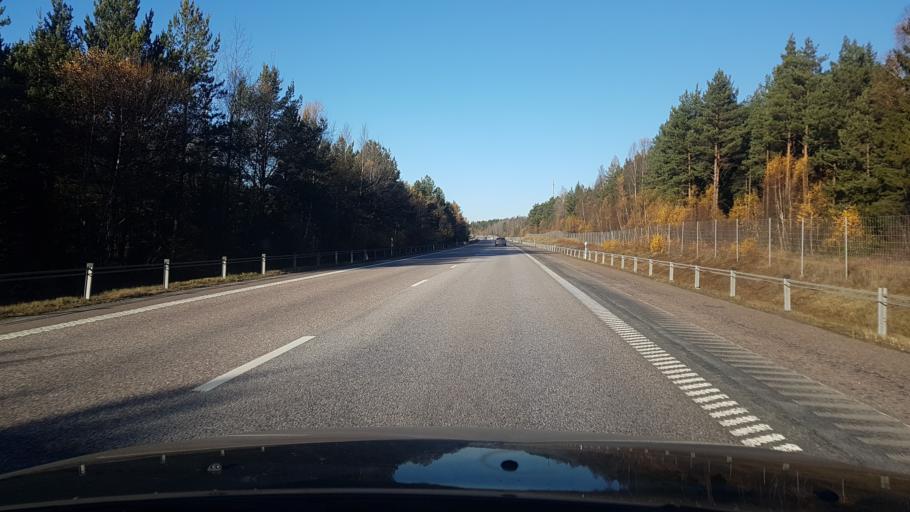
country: SE
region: Stockholm
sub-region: Sigtuna Kommun
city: Marsta
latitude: 59.6601
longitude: 17.8847
